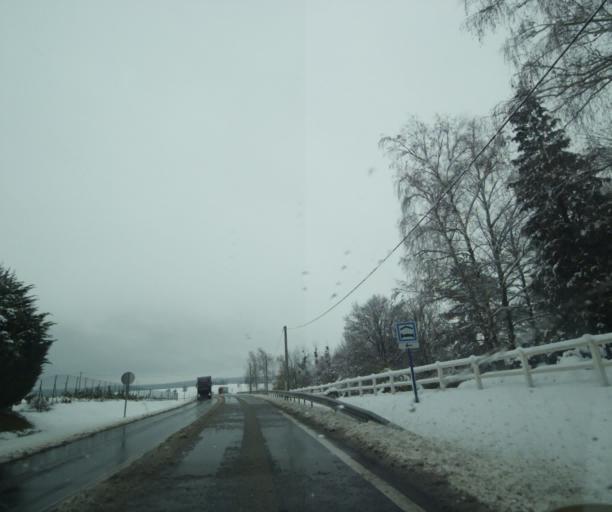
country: FR
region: Champagne-Ardenne
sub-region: Departement de la Haute-Marne
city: Montier-en-Der
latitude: 48.5197
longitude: 4.8098
